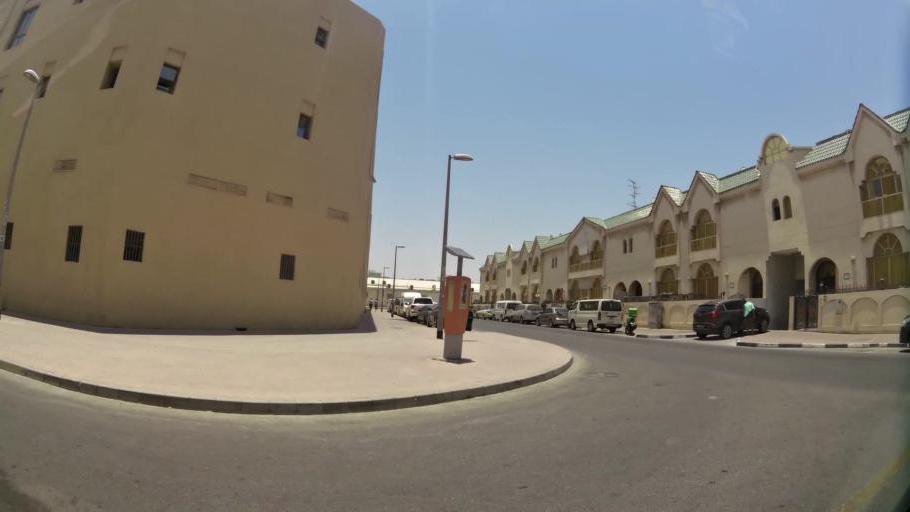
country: AE
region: Ash Shariqah
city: Sharjah
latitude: 25.2742
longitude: 55.3376
